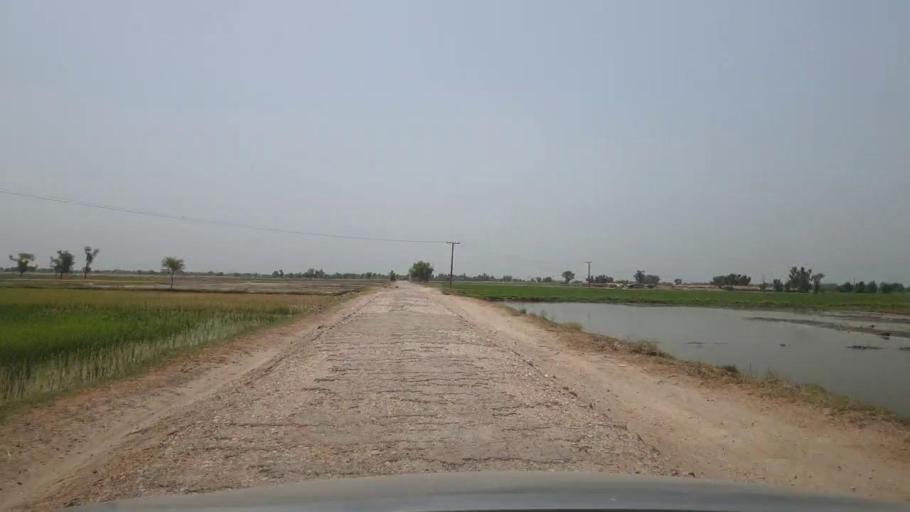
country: PK
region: Sindh
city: Garhi Yasin
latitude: 27.9170
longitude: 68.4039
